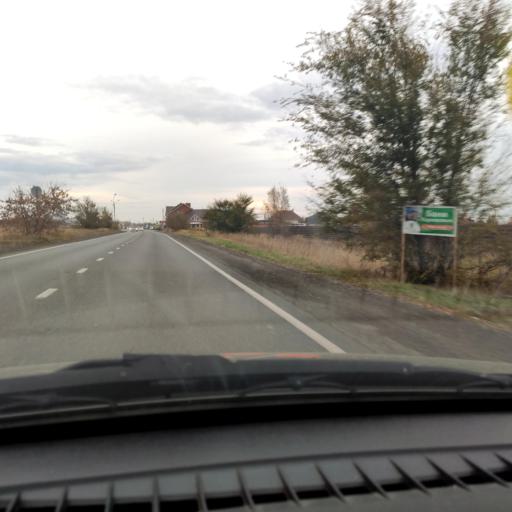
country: RU
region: Samara
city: Podstepki
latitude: 53.5176
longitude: 49.2115
